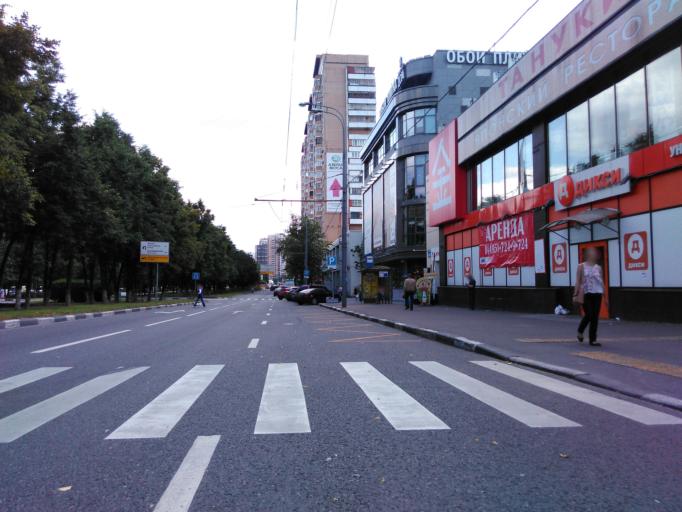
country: RU
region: Moskovskaya
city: Semenovskoye
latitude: 55.6810
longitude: 37.5569
